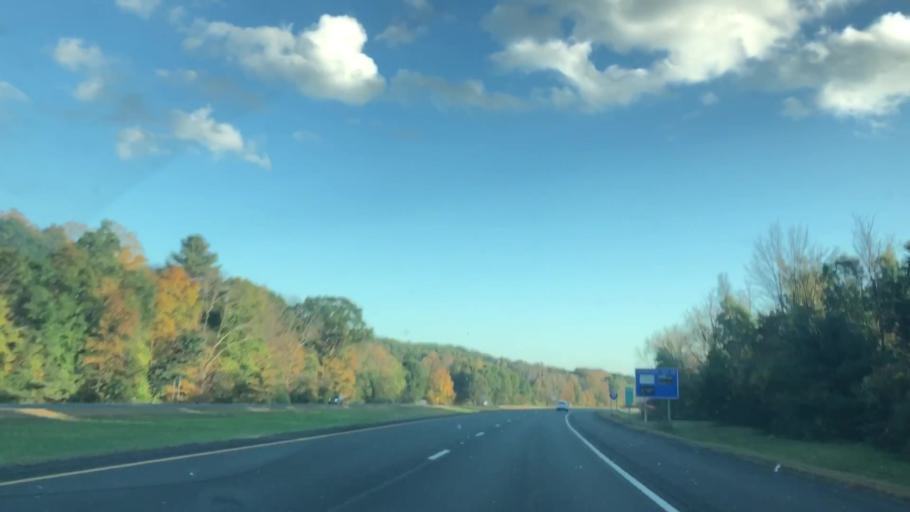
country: US
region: Massachusetts
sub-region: Franklin County
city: Bernardston
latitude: 42.6942
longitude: -72.5463
